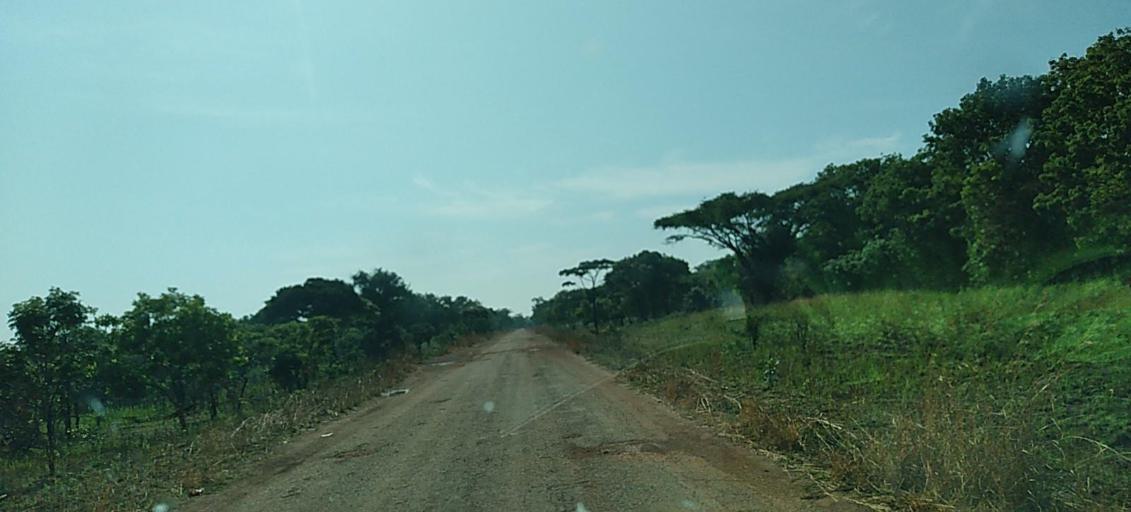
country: ZM
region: North-Western
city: Mwinilunga
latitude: -11.7905
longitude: 25.0639
